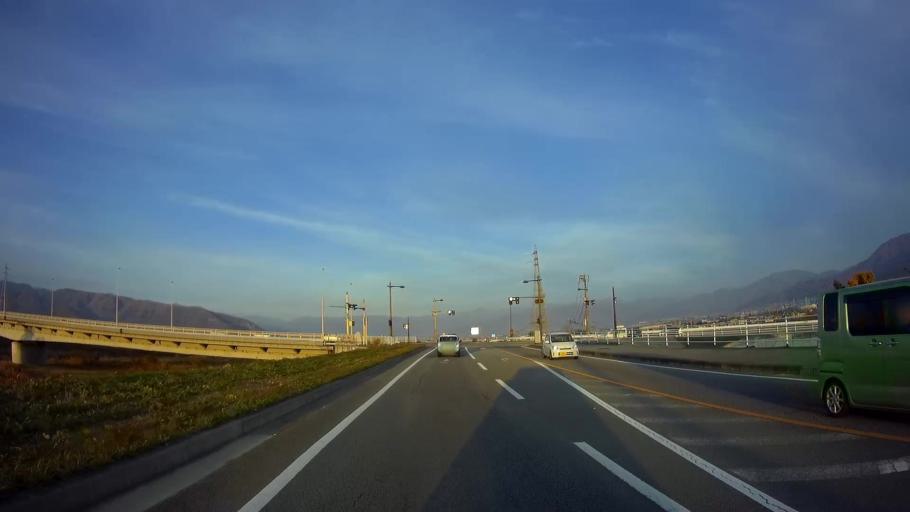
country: JP
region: Yamanashi
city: Isawa
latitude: 35.6078
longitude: 138.5910
